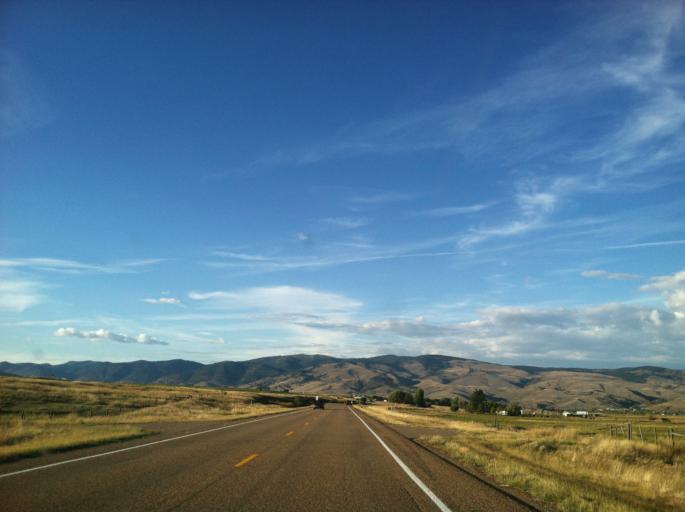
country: US
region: Montana
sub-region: Granite County
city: Philipsburg
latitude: 46.6303
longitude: -113.1702
